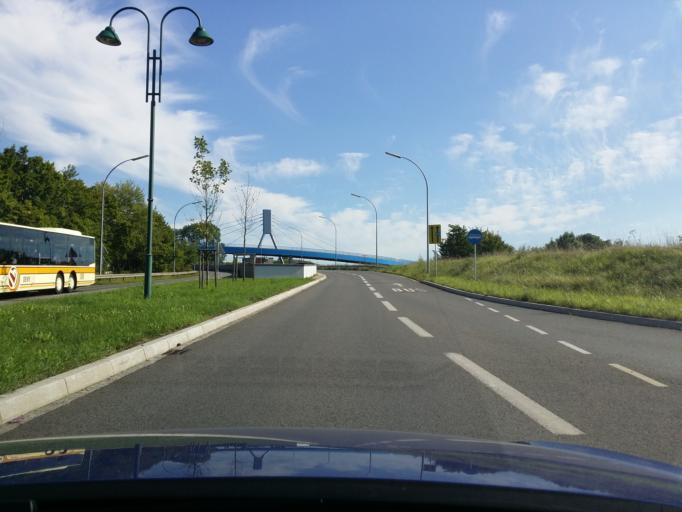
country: LU
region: Luxembourg
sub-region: Canton de Capellen
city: Mamer
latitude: 49.6233
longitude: 6.0373
